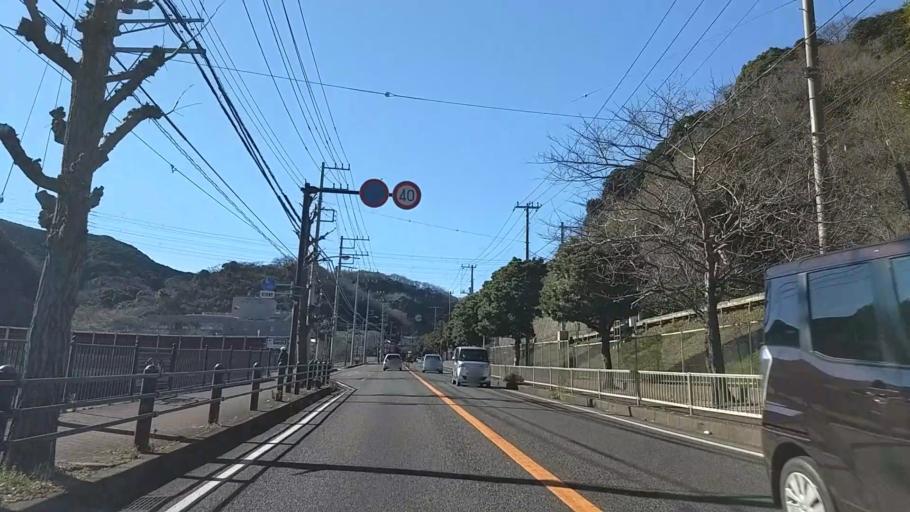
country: JP
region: Kanagawa
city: Yokosuka
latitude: 35.2250
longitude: 139.6992
